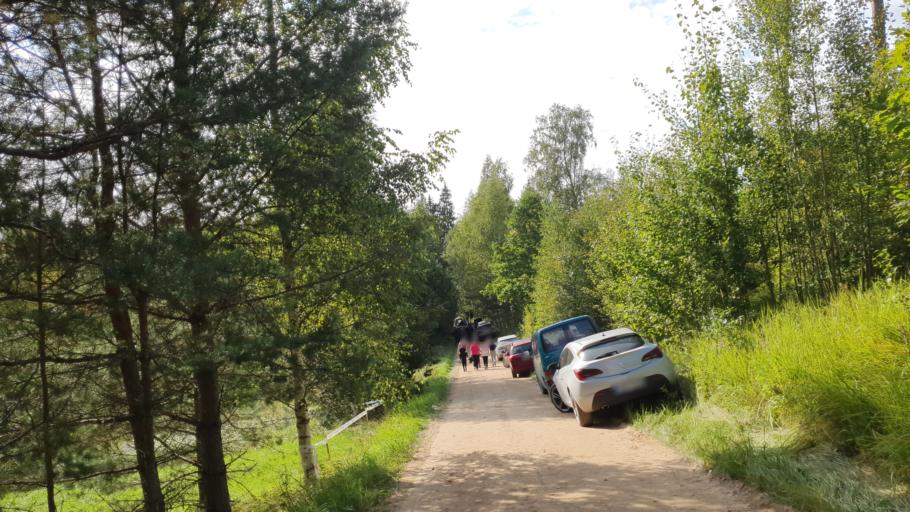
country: EE
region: Tartu
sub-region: UElenurme vald
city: Ulenurme
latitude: 58.1333
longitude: 26.7626
